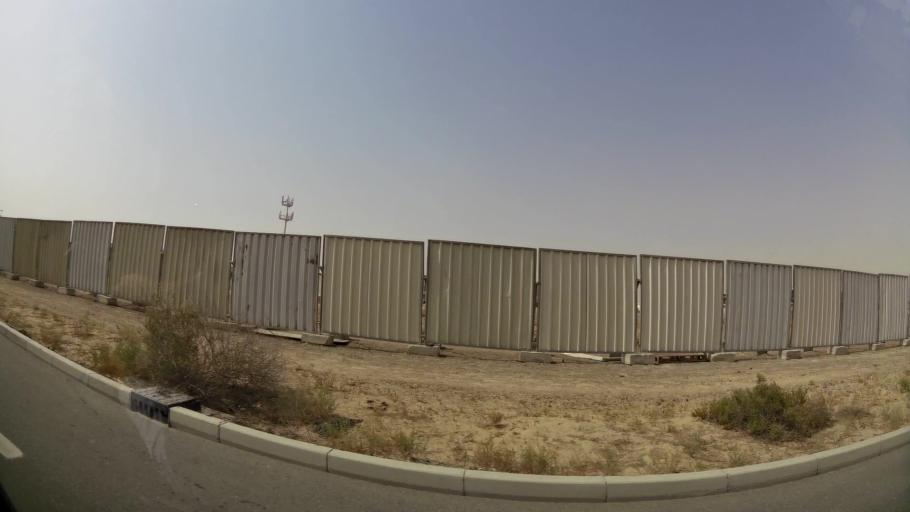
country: AE
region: Ash Shariqah
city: Sharjah
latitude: 25.2428
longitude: 55.4504
